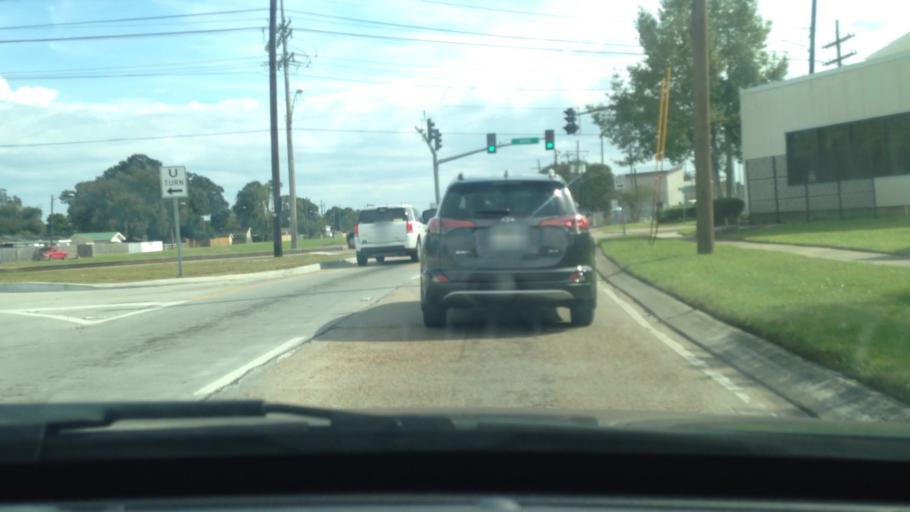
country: US
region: Louisiana
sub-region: Jefferson Parish
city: River Ridge
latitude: 29.9848
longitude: -90.2139
